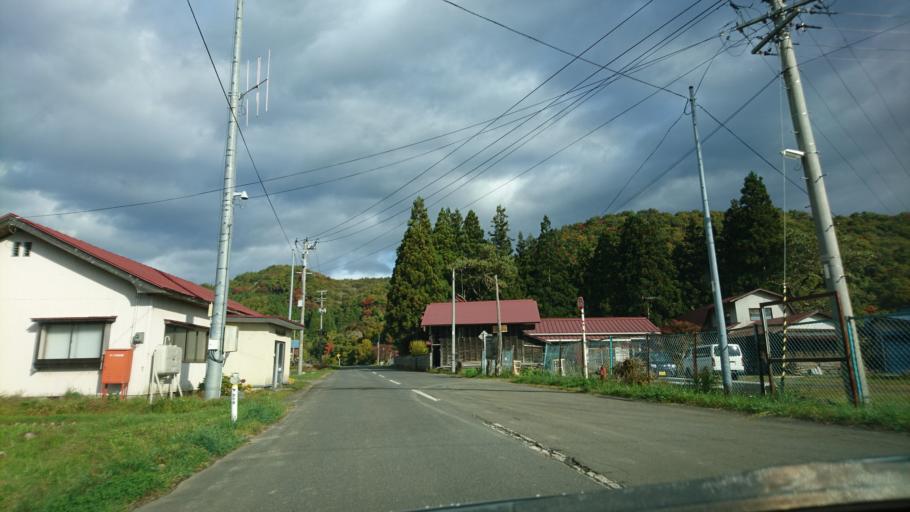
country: JP
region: Iwate
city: Mizusawa
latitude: 39.0963
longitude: 140.9723
